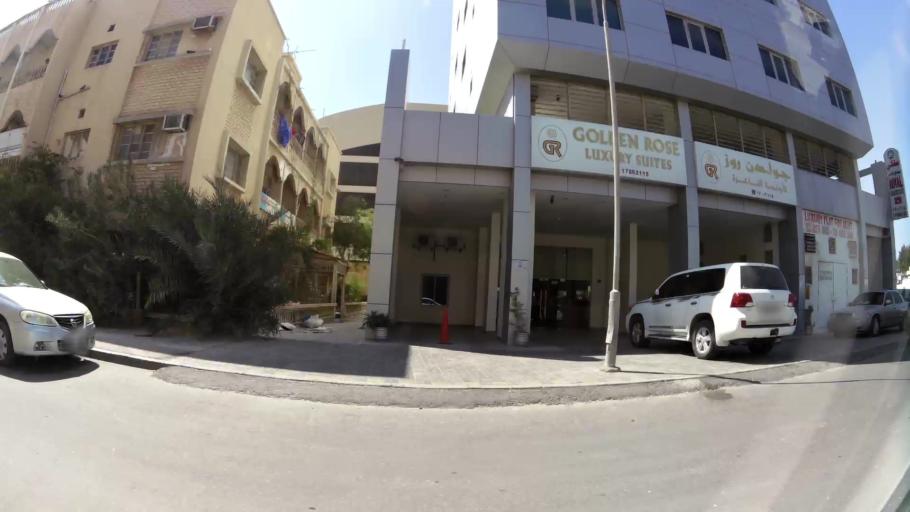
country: BH
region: Manama
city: Manama
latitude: 26.2043
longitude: 50.5997
